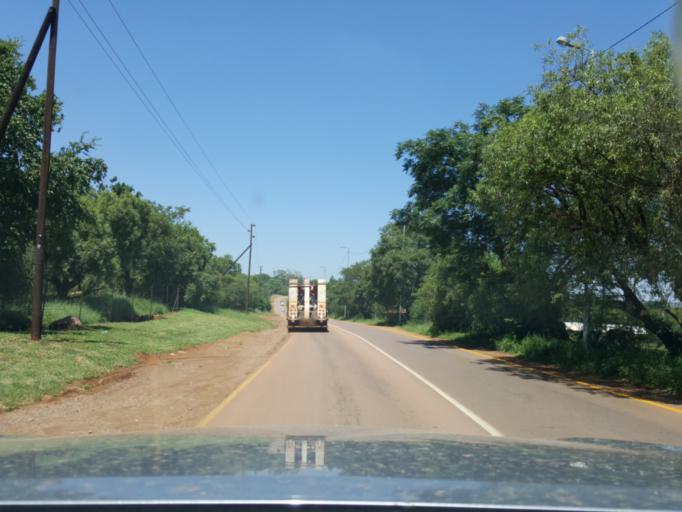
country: ZA
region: Gauteng
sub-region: City of Tshwane Metropolitan Municipality
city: Pretoria
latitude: -25.6609
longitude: 28.3109
